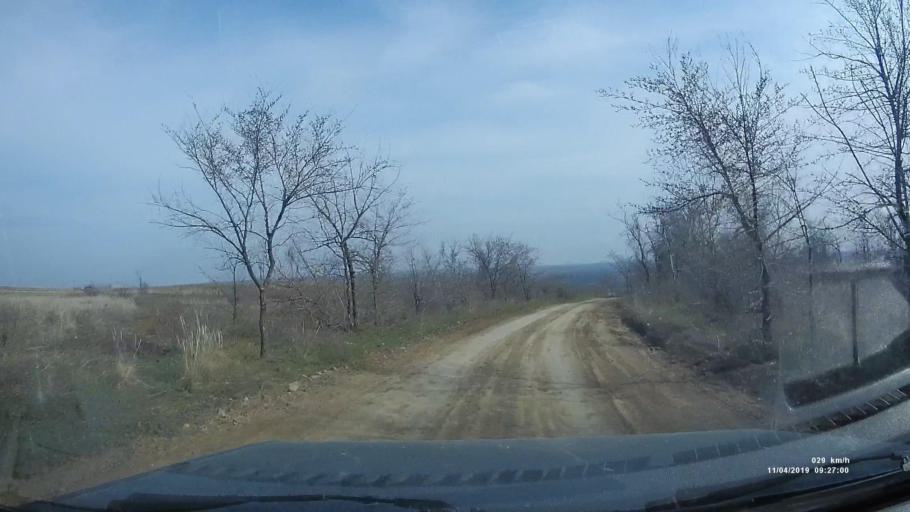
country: RU
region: Rostov
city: Staraya Stanitsa
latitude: 48.2648
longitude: 40.3651
